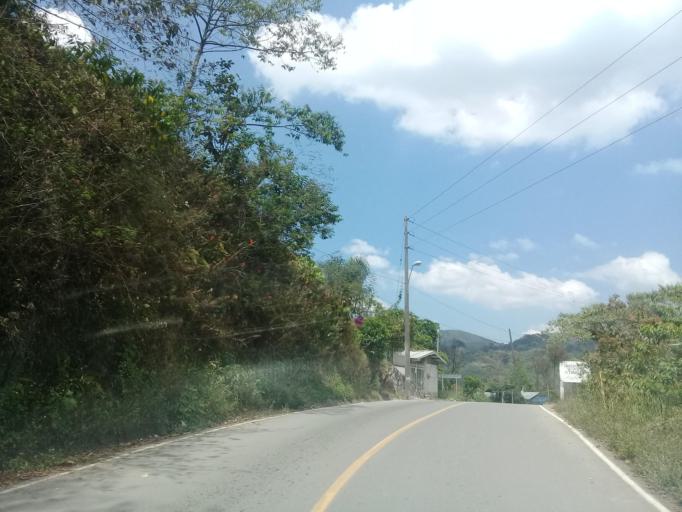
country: MX
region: Veracruz
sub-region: Tlilapan
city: Tonalixco
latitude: 18.7908
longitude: -97.0574
